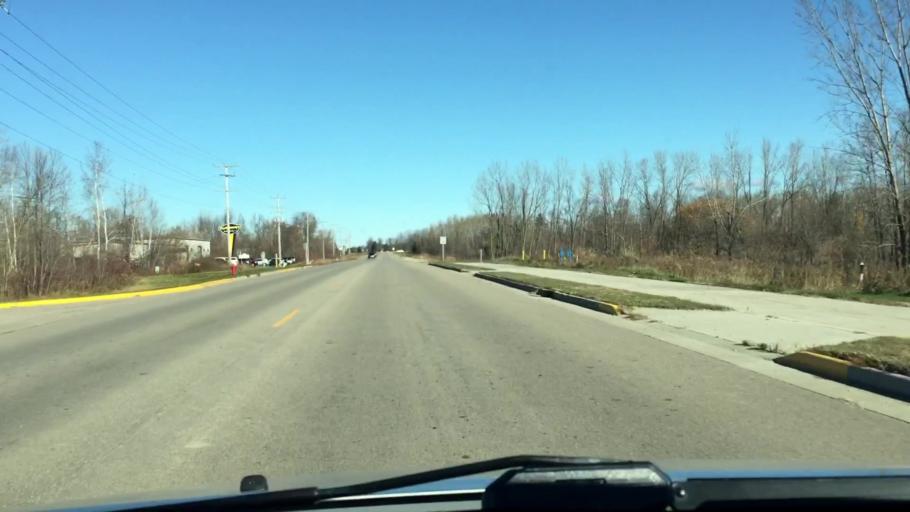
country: US
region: Wisconsin
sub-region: Brown County
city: Pulaski
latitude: 44.6816
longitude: -88.2427
